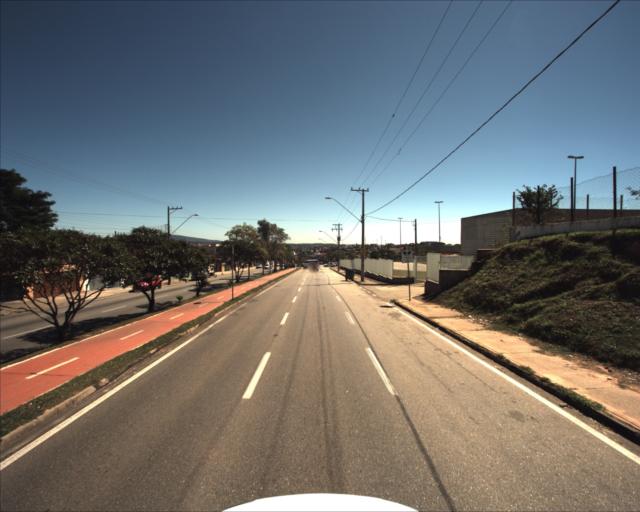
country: BR
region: Sao Paulo
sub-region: Sorocaba
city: Sorocaba
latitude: -23.4921
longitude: -47.4854
